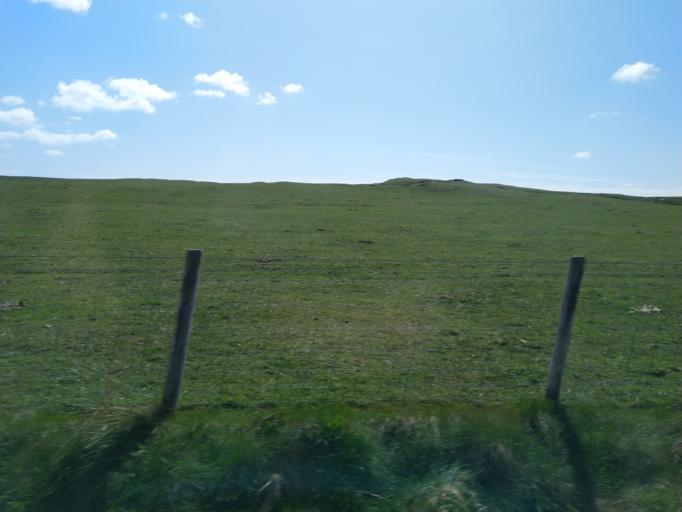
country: GB
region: Scotland
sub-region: Eilean Siar
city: Barra
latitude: 56.4839
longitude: -6.8908
